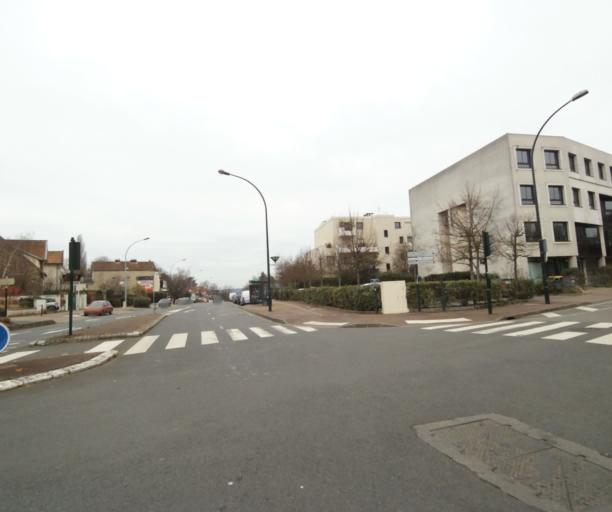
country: FR
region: Ile-de-France
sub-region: Departement des Hauts-de-Seine
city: Saint-Cloud
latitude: 48.8490
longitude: 2.2011
